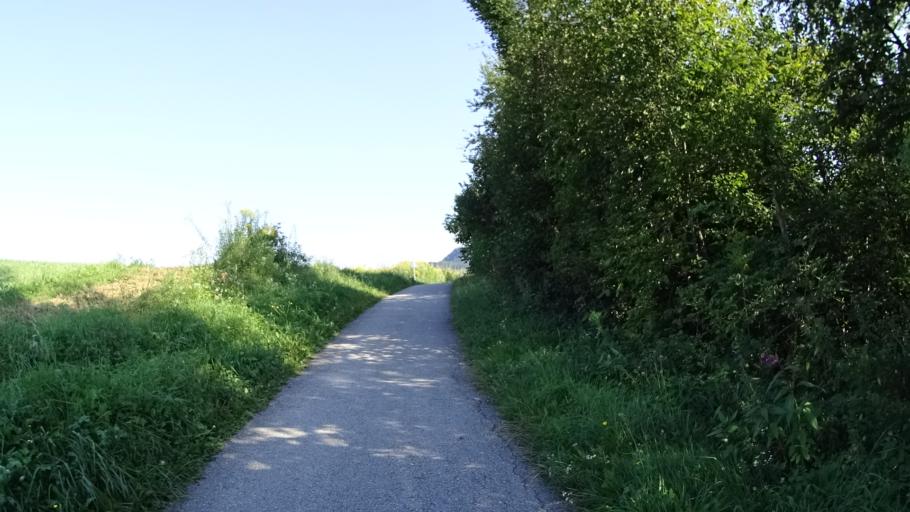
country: AT
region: Carinthia
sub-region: Politischer Bezirk Villach Land
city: Wernberg
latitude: 46.6038
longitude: 13.9456
